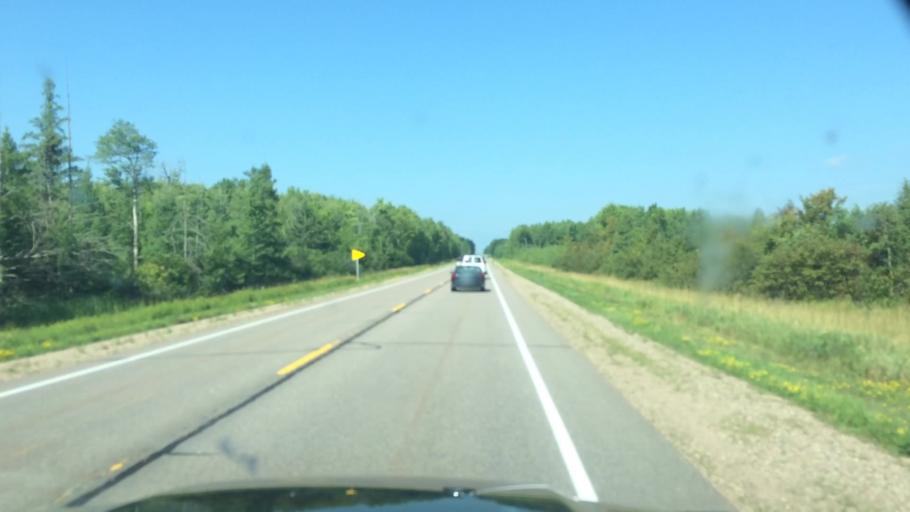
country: US
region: Wisconsin
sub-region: Langlade County
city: Antigo
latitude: 45.1469
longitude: -89.3700
